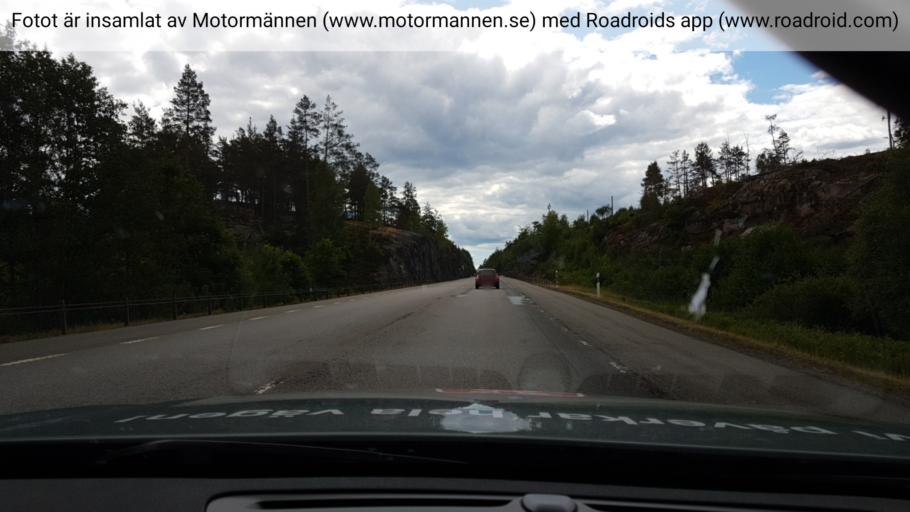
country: SE
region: Kalmar
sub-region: Vasterviks Kommun
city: Ankarsrum
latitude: 57.6014
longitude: 16.4804
